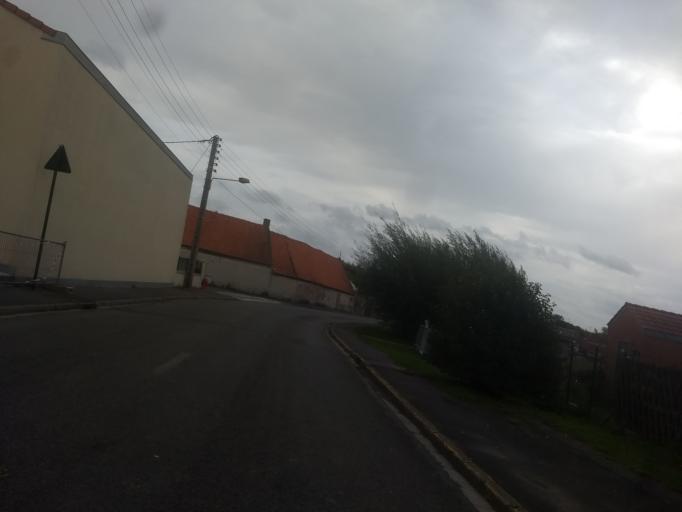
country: FR
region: Nord-Pas-de-Calais
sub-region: Departement du Pas-de-Calais
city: Achicourt
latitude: 50.2741
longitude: 2.7546
